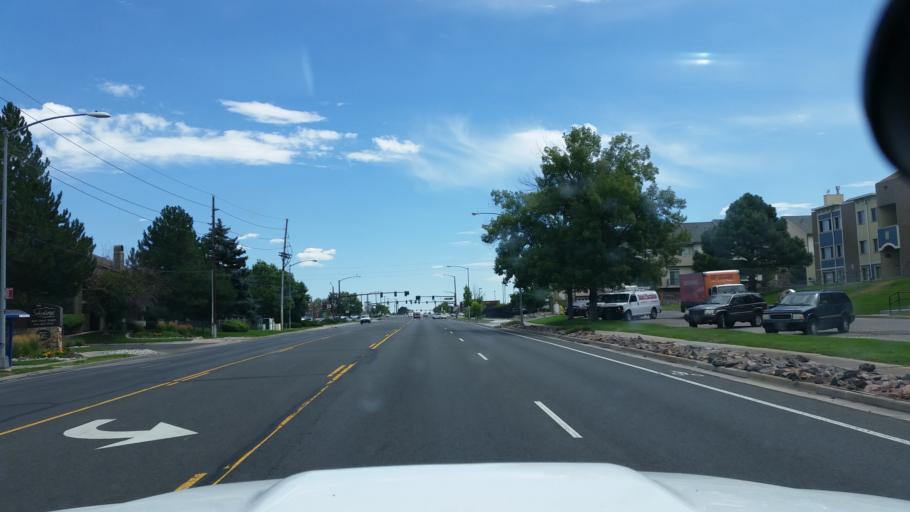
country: US
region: Colorado
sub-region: Adams County
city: Thornton
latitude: 39.8562
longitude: -104.9817
